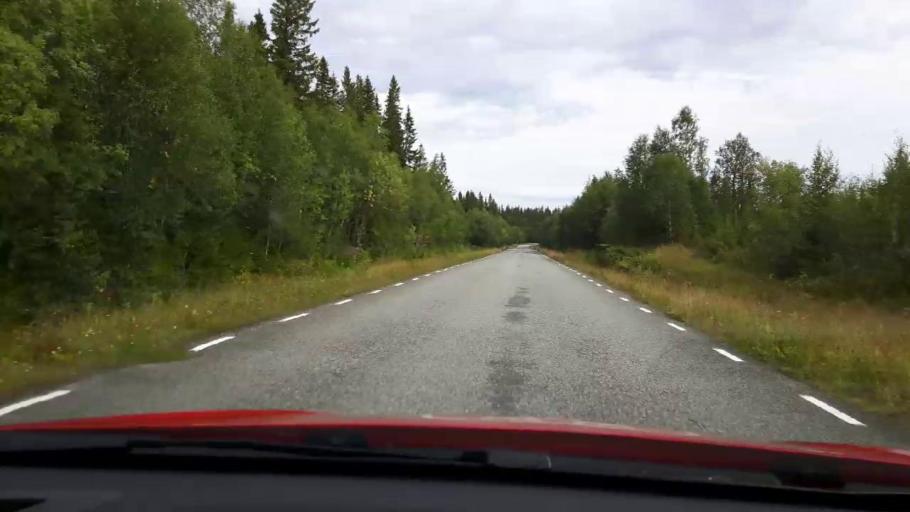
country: SE
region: Jaemtland
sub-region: Are Kommun
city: Are
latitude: 63.7345
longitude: 13.0112
